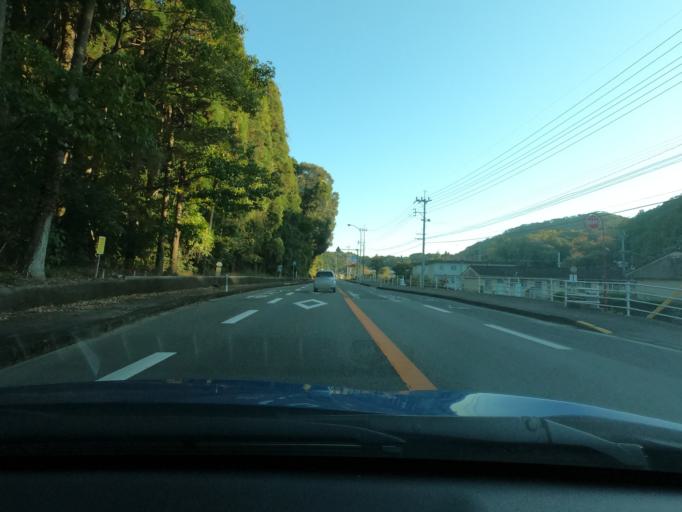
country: JP
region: Kagoshima
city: Satsumasendai
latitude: 31.8493
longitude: 130.2680
